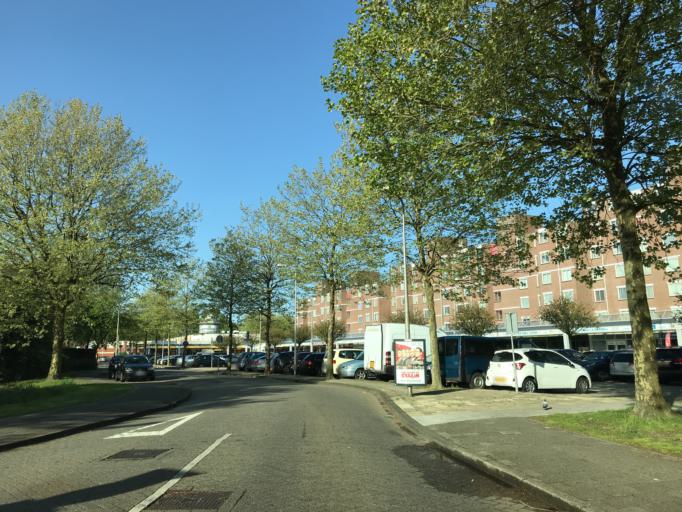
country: NL
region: North Holland
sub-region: Gemeente Diemen
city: Diemen
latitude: 52.3344
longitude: 4.9587
